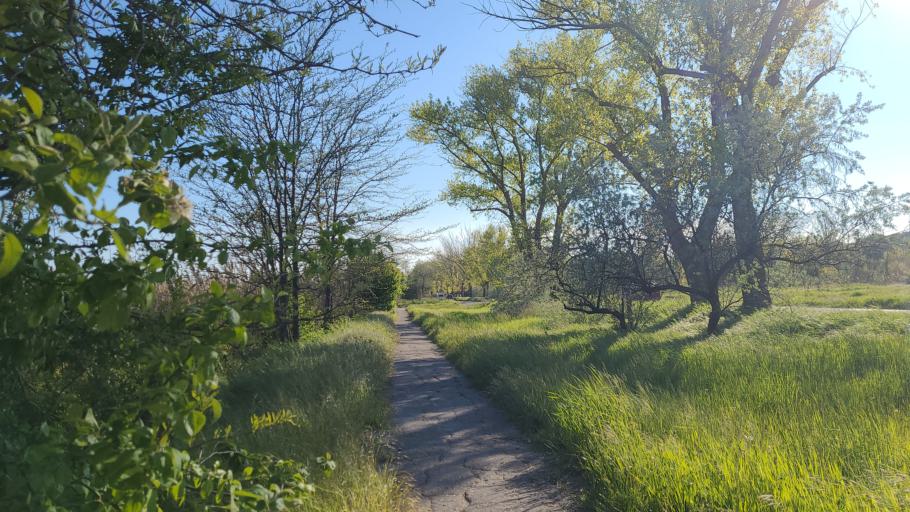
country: RU
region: Krasnodarskiy
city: Tsibanobalka
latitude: 44.9488
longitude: 37.3096
